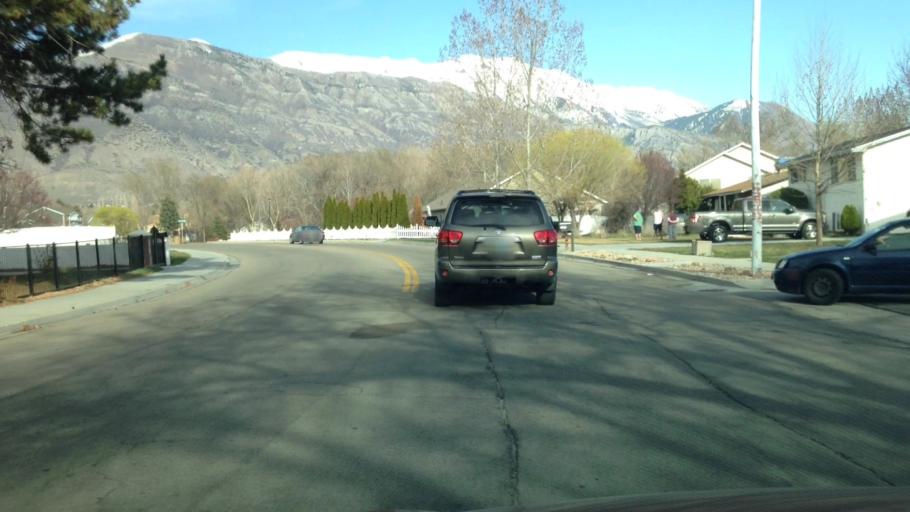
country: US
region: Utah
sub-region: Utah County
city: American Fork
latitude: 40.3910
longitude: -111.7880
